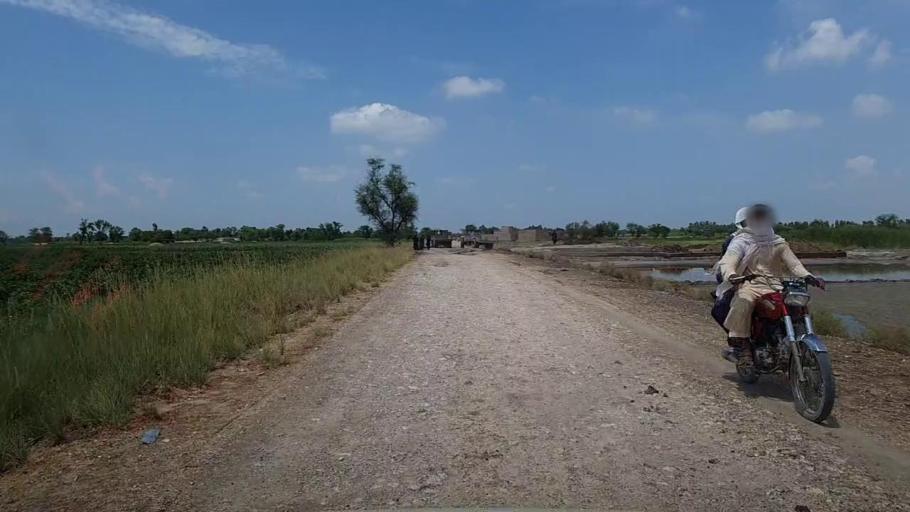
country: PK
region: Sindh
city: Bhiria
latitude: 26.9722
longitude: 68.2396
